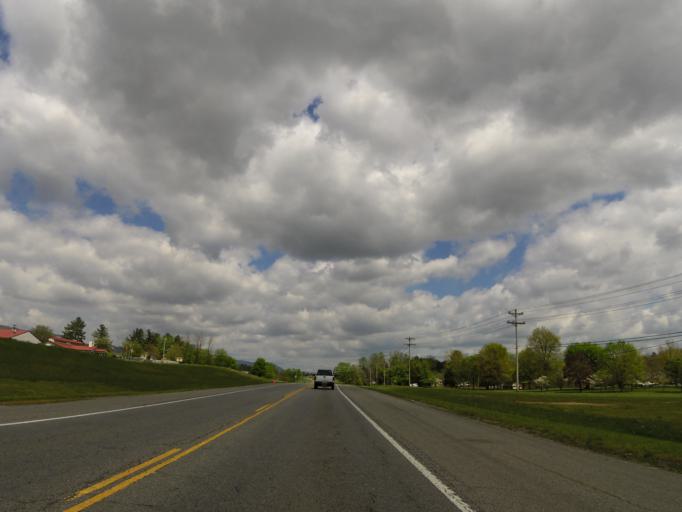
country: US
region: Tennessee
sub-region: Campbell County
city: Fincastle
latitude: 36.4042
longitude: -84.0713
